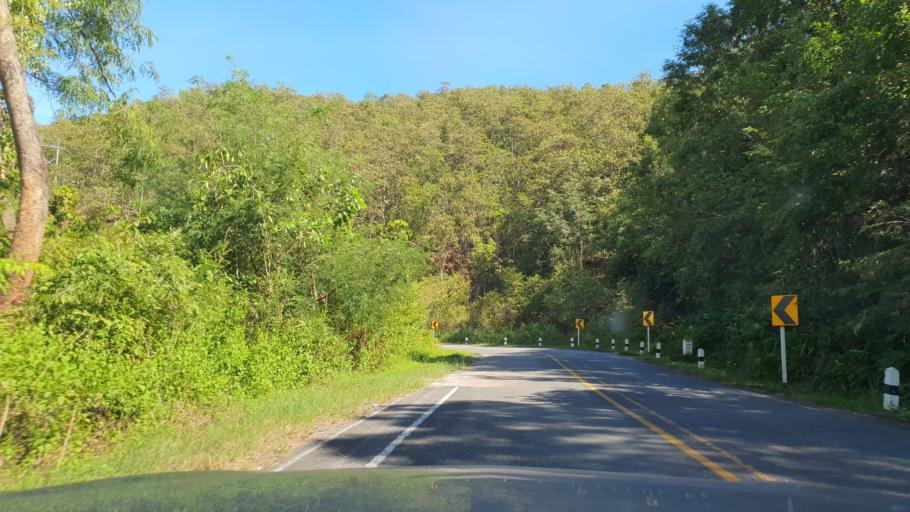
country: TH
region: Chiang Mai
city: Phrao
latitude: 19.3689
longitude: 99.2459
